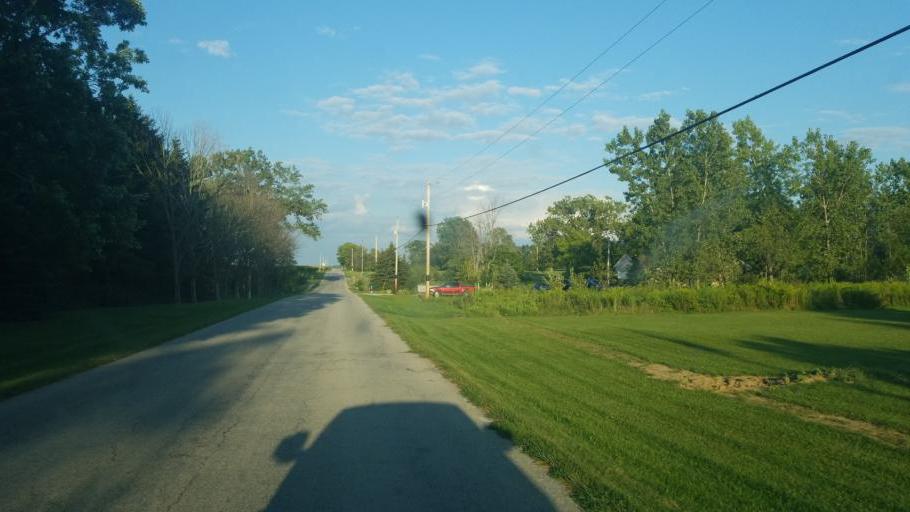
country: US
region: Ohio
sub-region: Huron County
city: Plymouth
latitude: 41.0522
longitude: -82.6452
